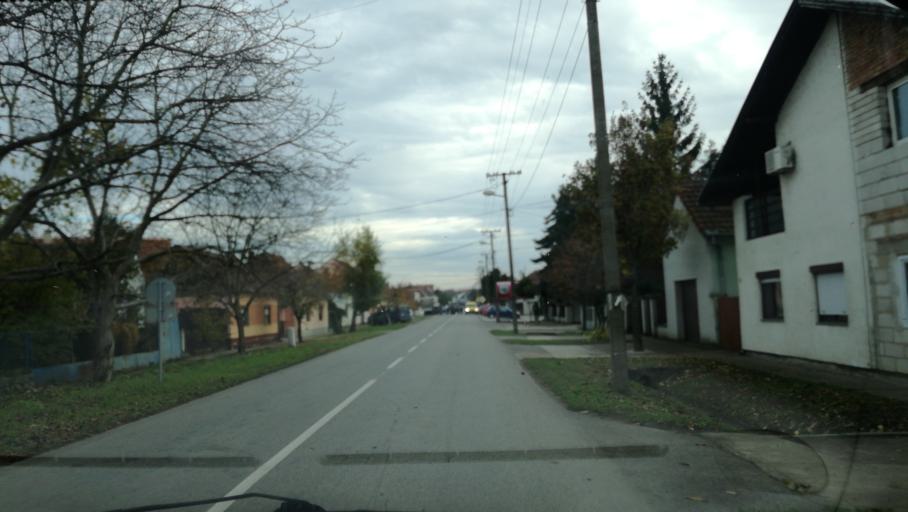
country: RS
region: Autonomna Pokrajina Vojvodina
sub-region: Severnobanatski Okrug
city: Kikinda
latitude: 45.8398
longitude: 20.4689
